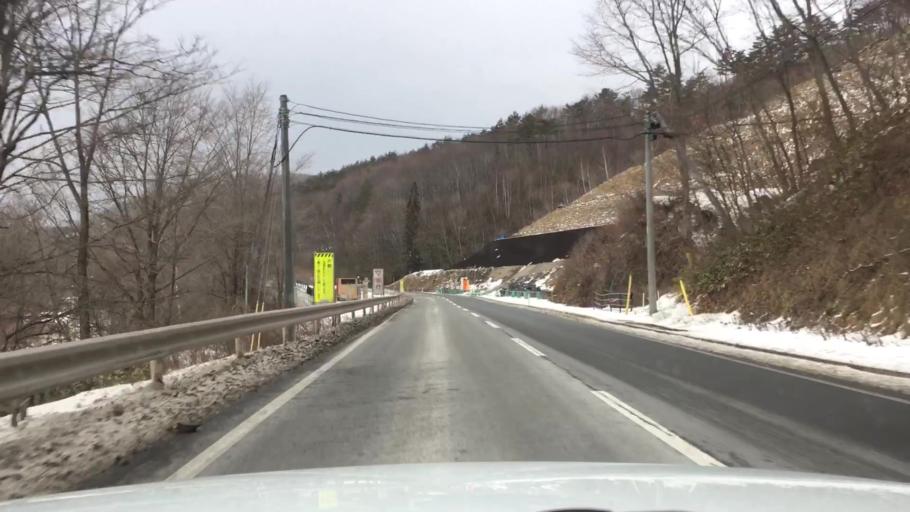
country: JP
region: Iwate
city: Morioka-shi
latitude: 39.6351
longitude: 141.4389
